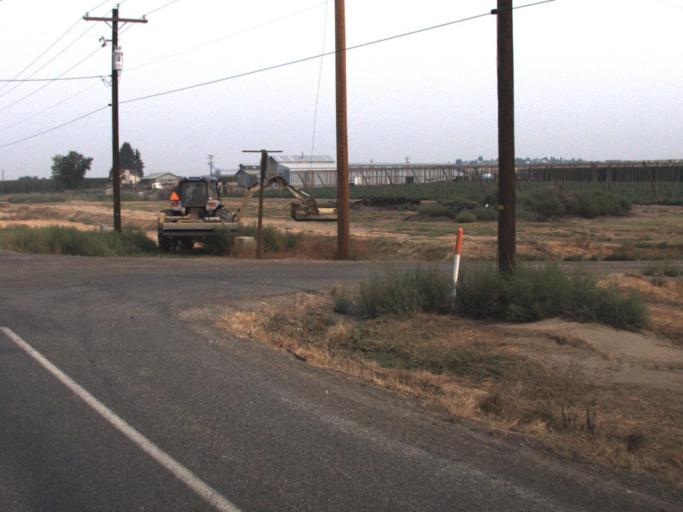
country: US
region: Washington
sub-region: Yakima County
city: Mabton
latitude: 46.2398
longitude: -119.9995
